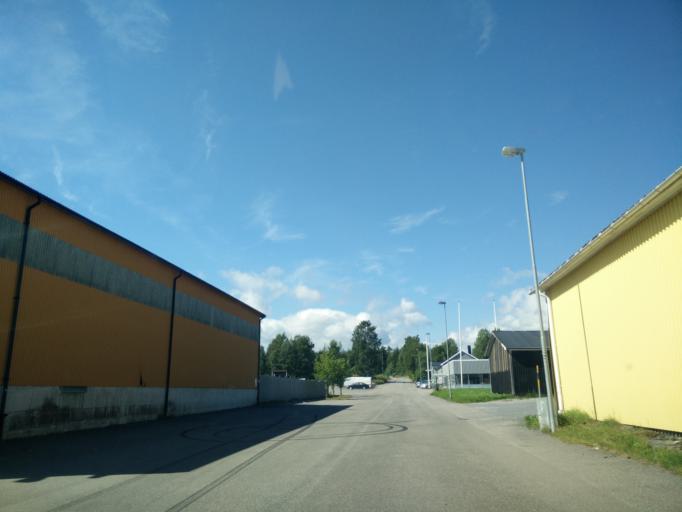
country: SE
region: Vaesternorrland
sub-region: Haernoesands Kommun
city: Haernoesand
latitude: 62.6304
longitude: 17.9116
